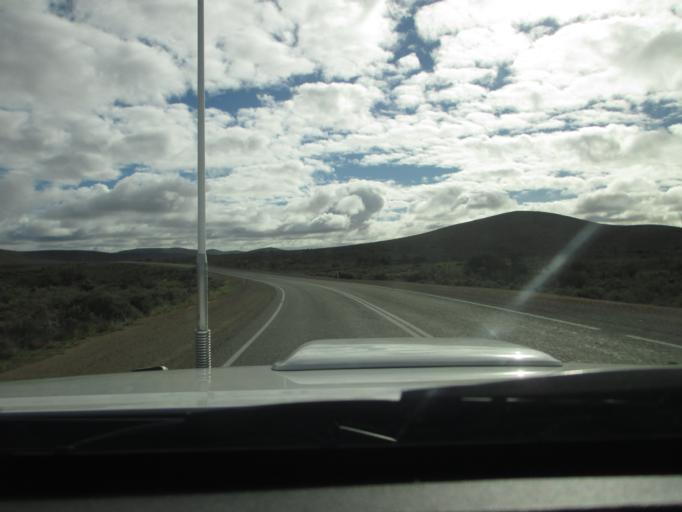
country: AU
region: South Australia
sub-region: Flinders Ranges
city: Quorn
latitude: -32.2487
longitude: 138.5141
